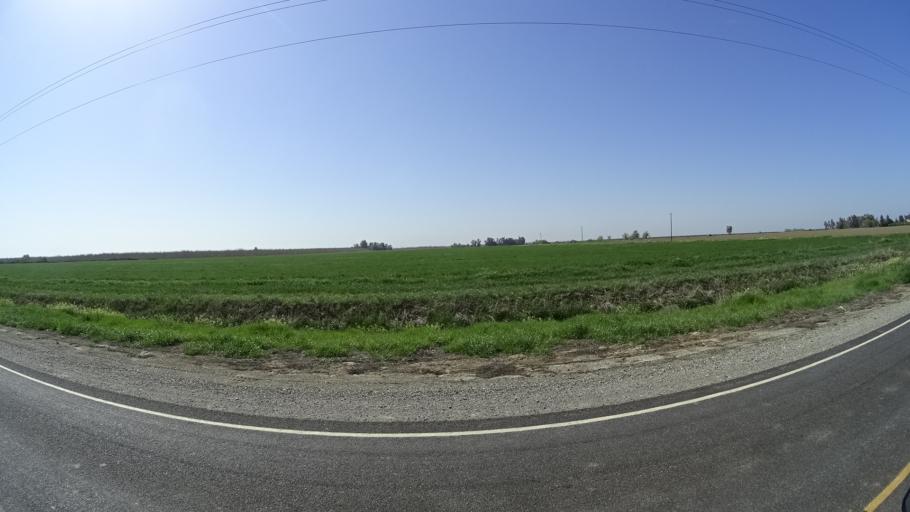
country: US
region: California
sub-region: Glenn County
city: Hamilton City
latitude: 39.6597
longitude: -122.0388
